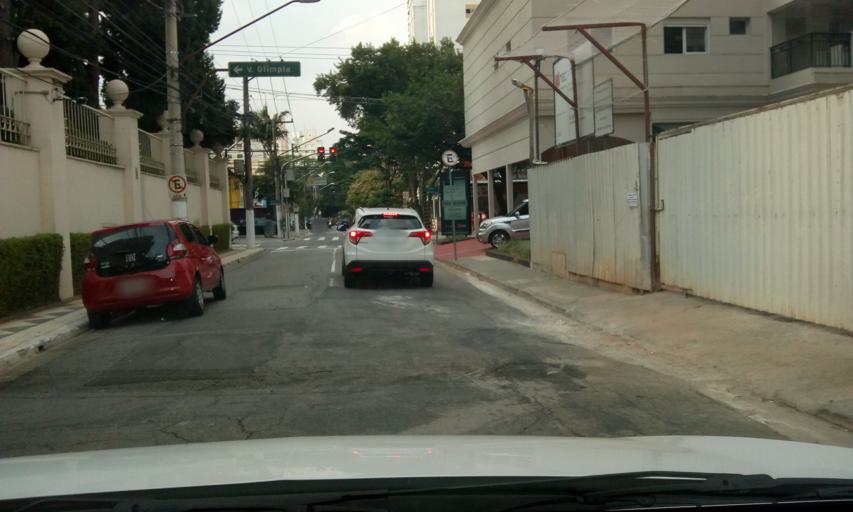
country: BR
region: Sao Paulo
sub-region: Sao Paulo
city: Sao Paulo
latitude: -23.6062
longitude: -46.6730
